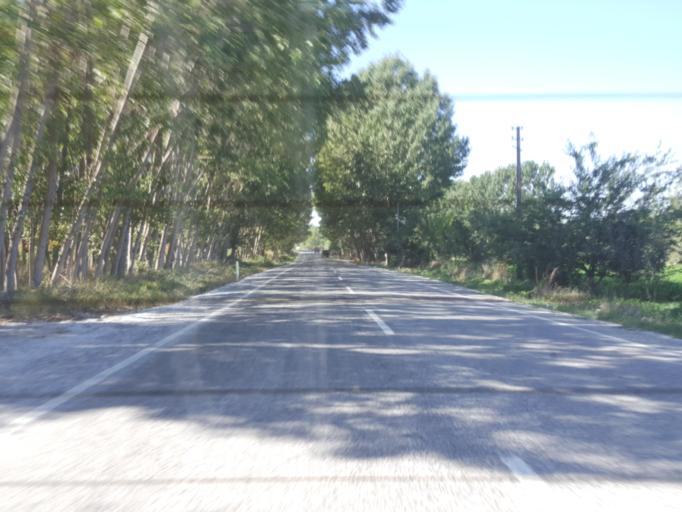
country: TR
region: Tokat
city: Pazar
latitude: 40.2745
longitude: 36.2646
